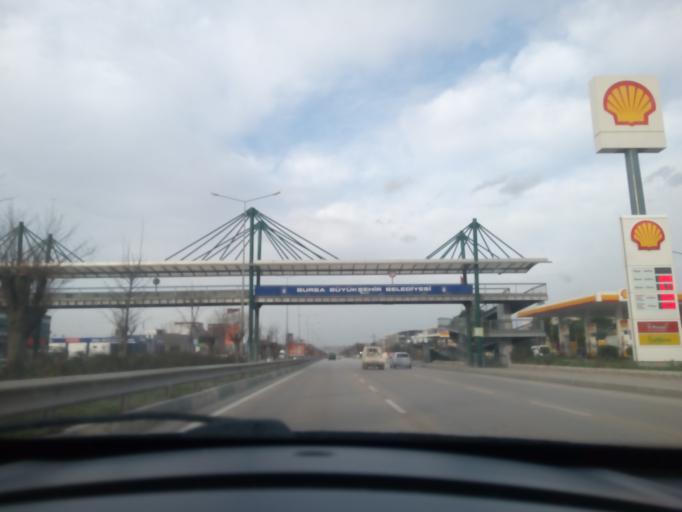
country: TR
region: Bursa
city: Cali
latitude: 40.2126
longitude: 28.9306
